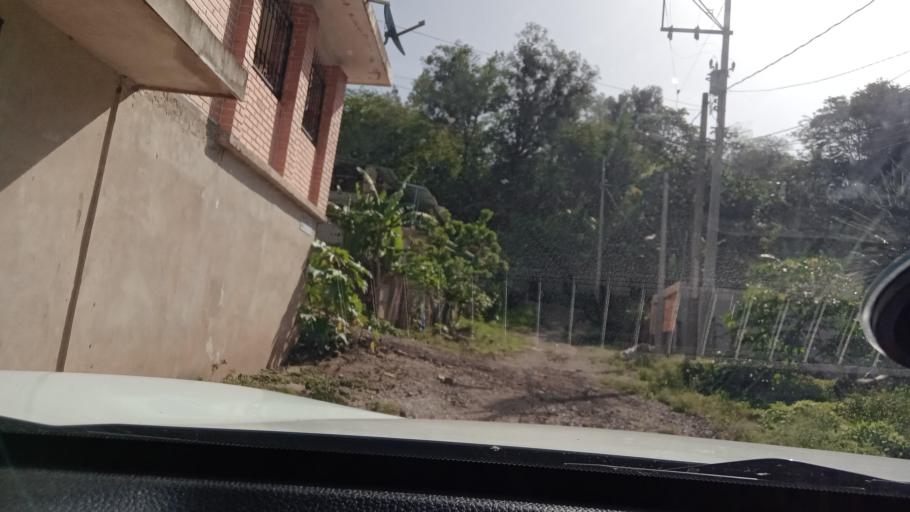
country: MX
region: Veracruz
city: El Castillo
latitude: 19.5660
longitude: -96.8614
